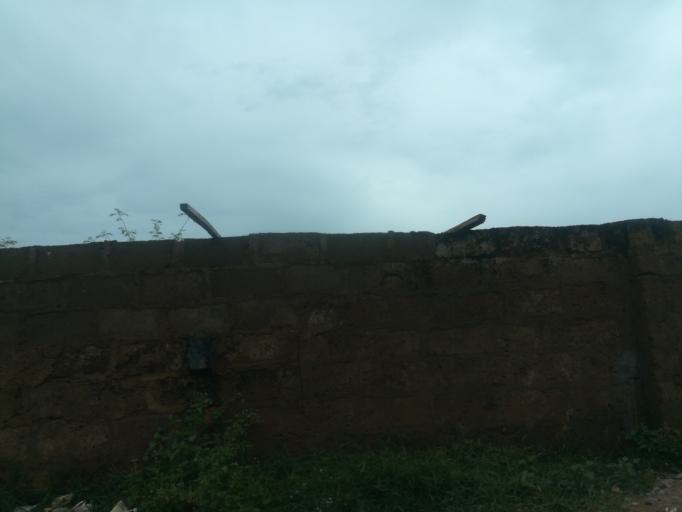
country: NG
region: Oyo
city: Ibadan
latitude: 7.3917
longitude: 3.9422
